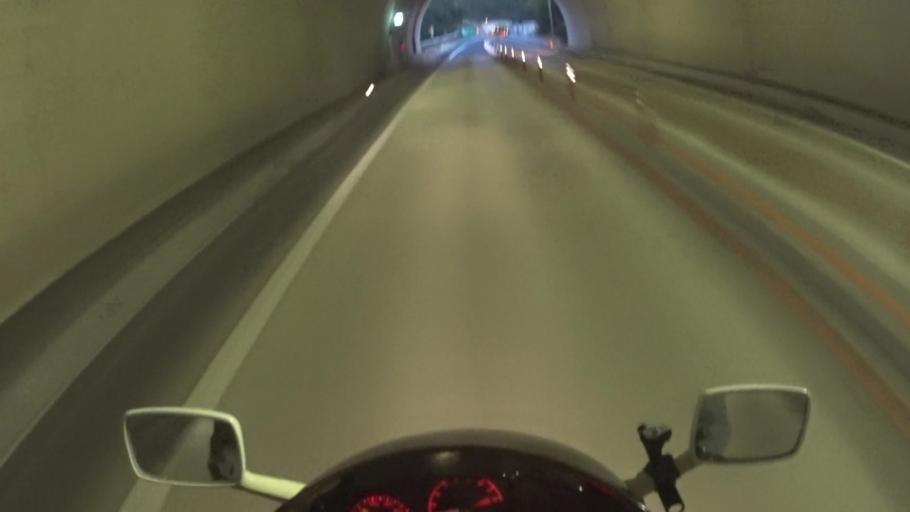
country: JP
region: Kyoto
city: Miyazu
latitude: 35.5438
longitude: 135.1544
